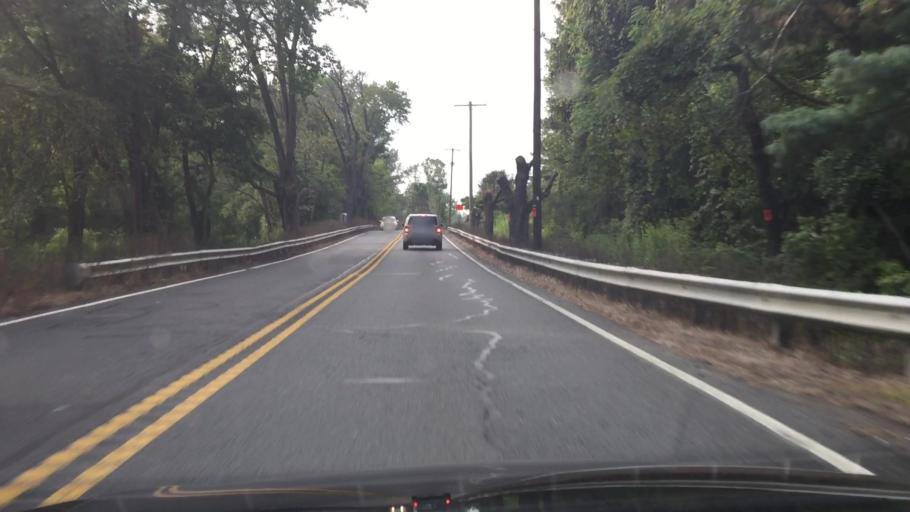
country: US
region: New Jersey
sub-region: Hunterdon County
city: Lambertville
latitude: 40.3229
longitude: -74.9155
